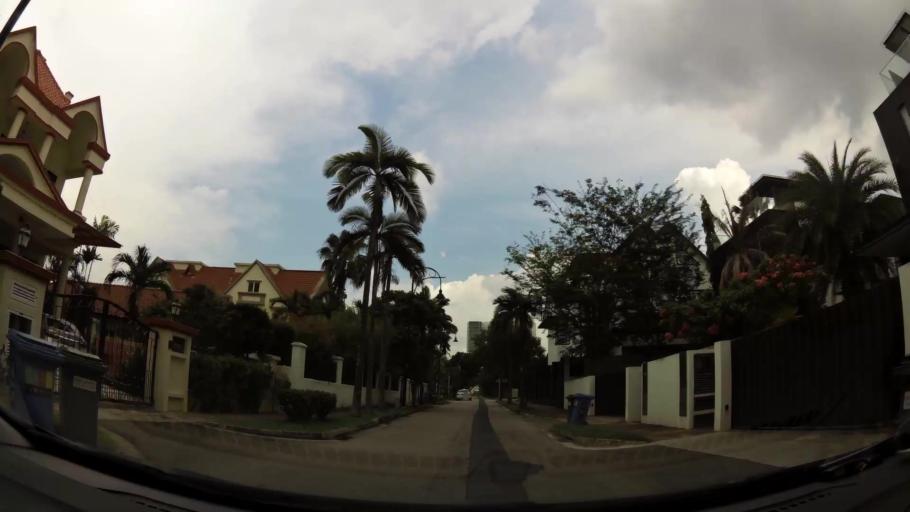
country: SG
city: Singapore
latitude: 1.3459
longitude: 103.8610
